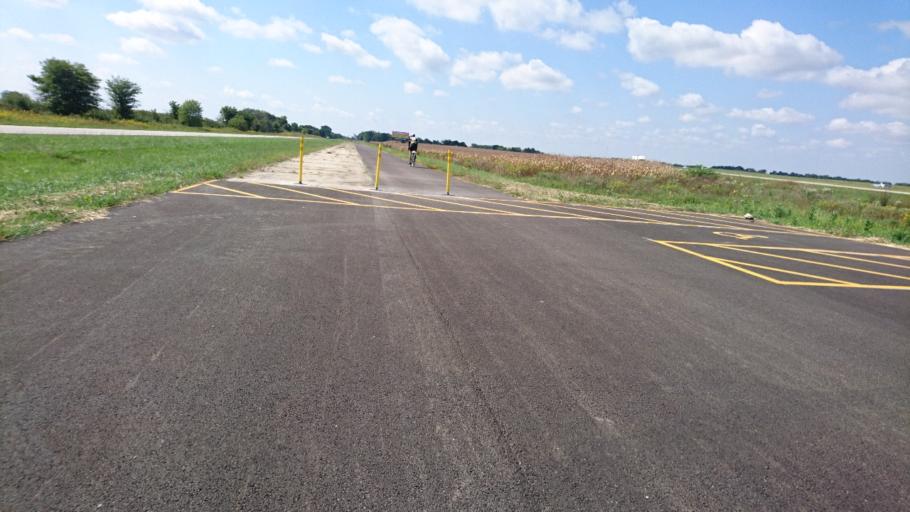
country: US
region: Illinois
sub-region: McLean County
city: Lexington
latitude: 40.5890
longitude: -88.8616
